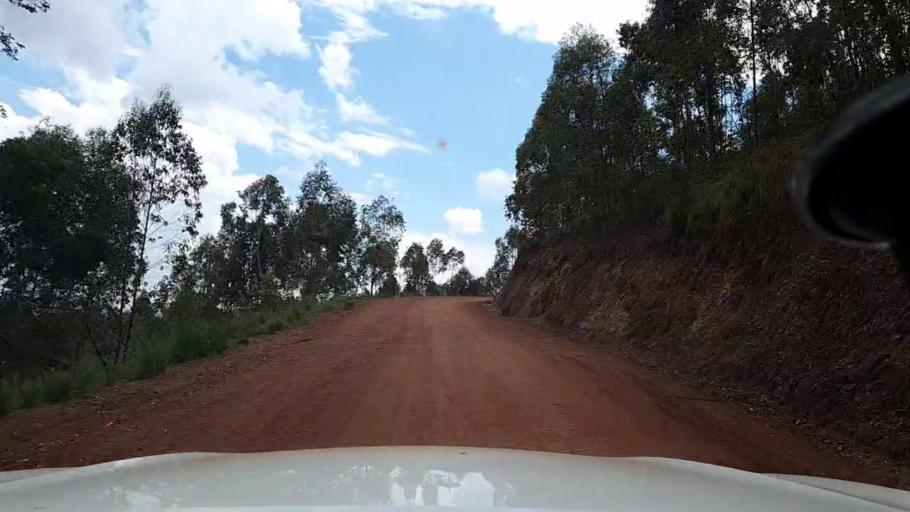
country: RW
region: Northern Province
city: Byumba
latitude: -1.7575
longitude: 29.8458
